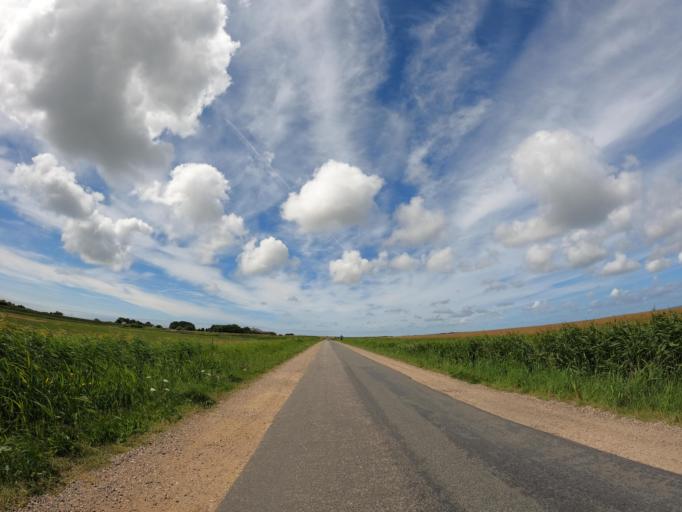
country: DE
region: Schleswig-Holstein
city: Sylt-Ost
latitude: 54.8754
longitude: 8.4204
